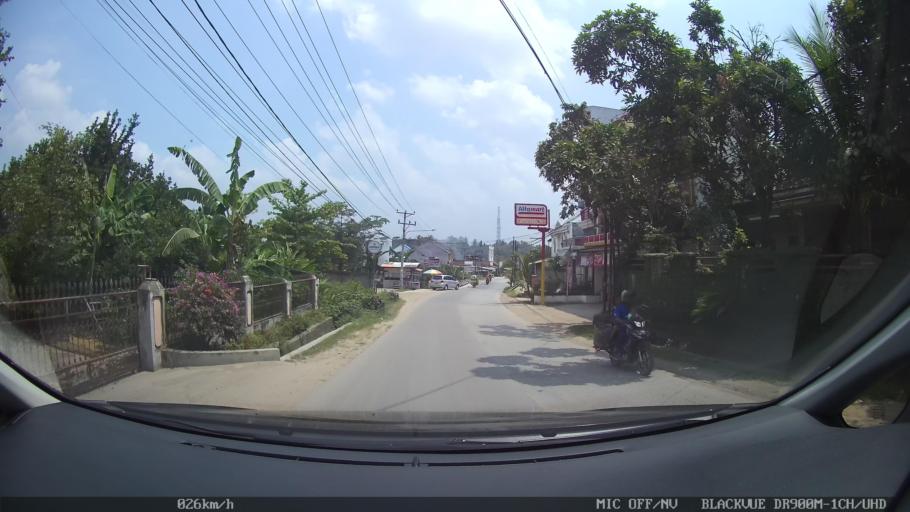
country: ID
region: Lampung
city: Pringsewu
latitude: -5.3434
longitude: 104.9747
